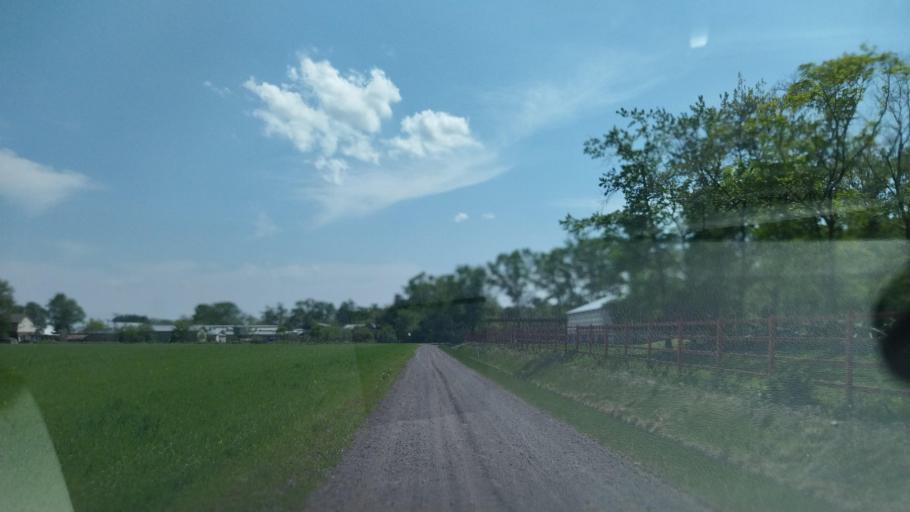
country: JP
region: Hokkaido
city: Otofuke
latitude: 43.1337
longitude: 143.2183
